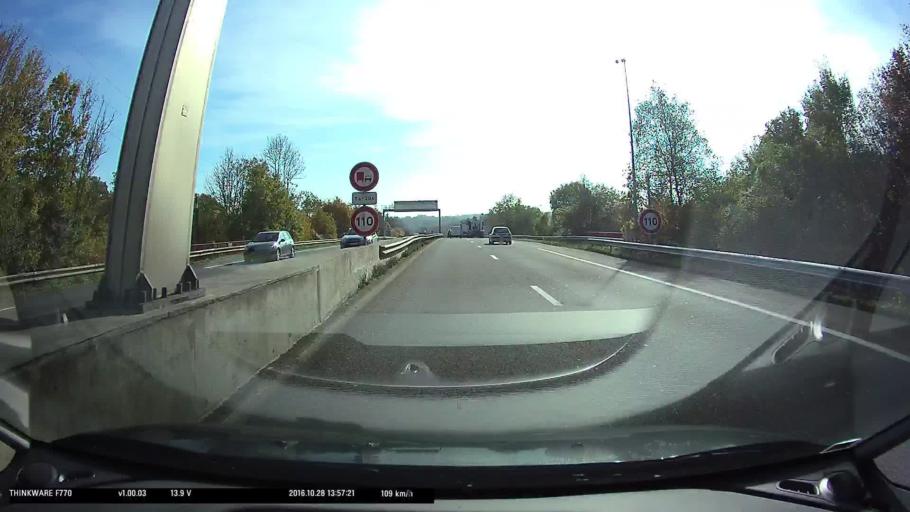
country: FR
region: Lorraine
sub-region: Departement de Meurthe-et-Moselle
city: Villers-les-Nancy
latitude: 48.6603
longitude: 6.1254
